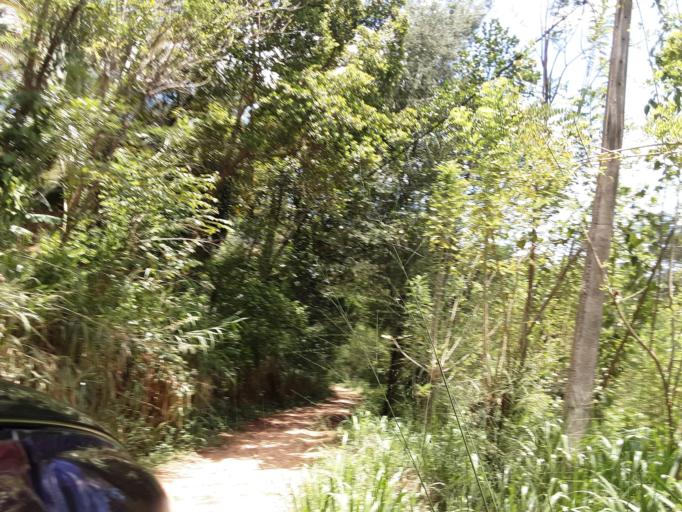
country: LK
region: Uva
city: Haputale
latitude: 6.8121
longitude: 81.1089
